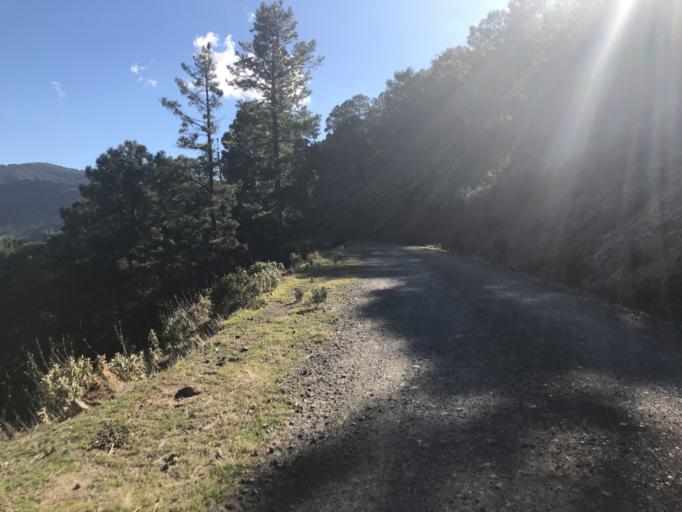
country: ES
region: Andalusia
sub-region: Provincia de Malaga
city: Tolox
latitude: 36.6784
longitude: -4.9266
